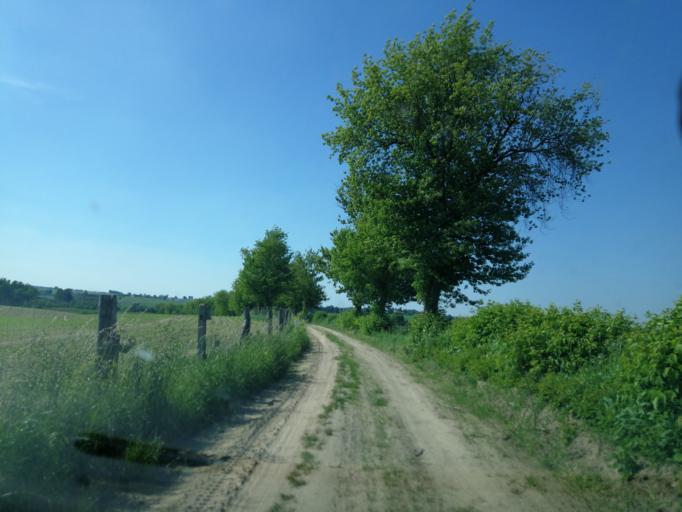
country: PL
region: Kujawsko-Pomorskie
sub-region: Powiat brodnicki
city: Bartniczka
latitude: 53.2372
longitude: 19.5860
